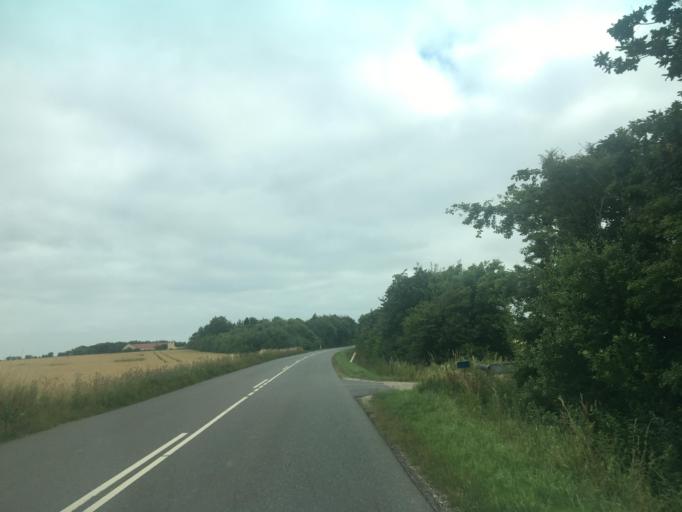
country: DK
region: North Denmark
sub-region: Thisted Kommune
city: Thisted
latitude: 56.8435
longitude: 8.5896
